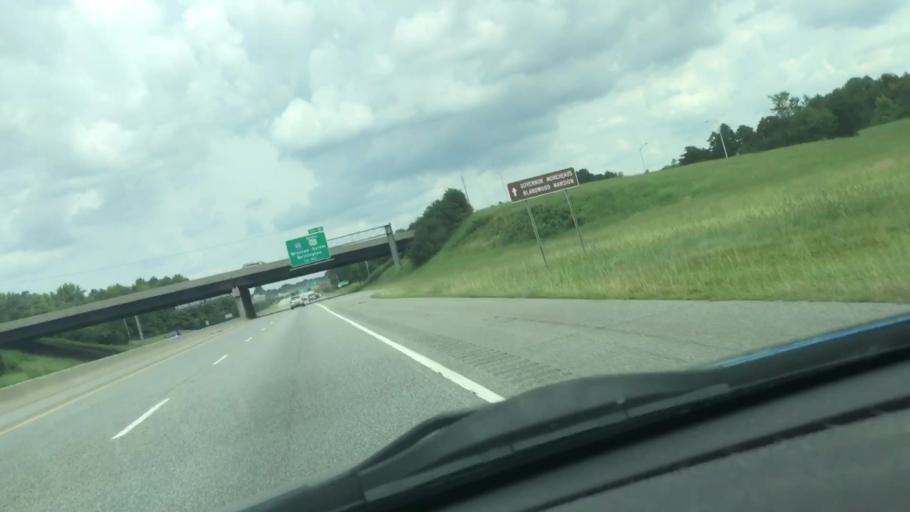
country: US
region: North Carolina
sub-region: Guilford County
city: Greensboro
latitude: 36.0266
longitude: -79.8243
